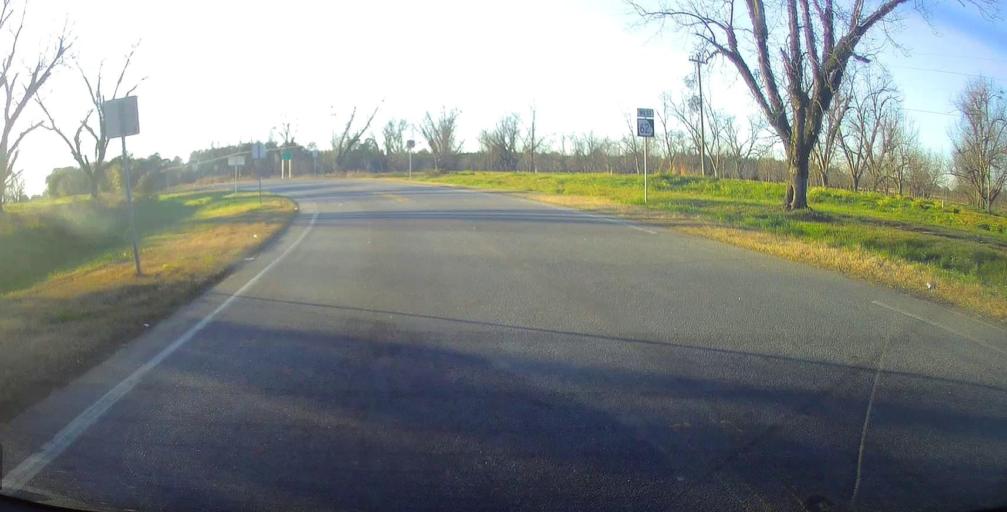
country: US
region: Georgia
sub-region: Dougherty County
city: Albany
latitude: 31.5040
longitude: -84.2110
